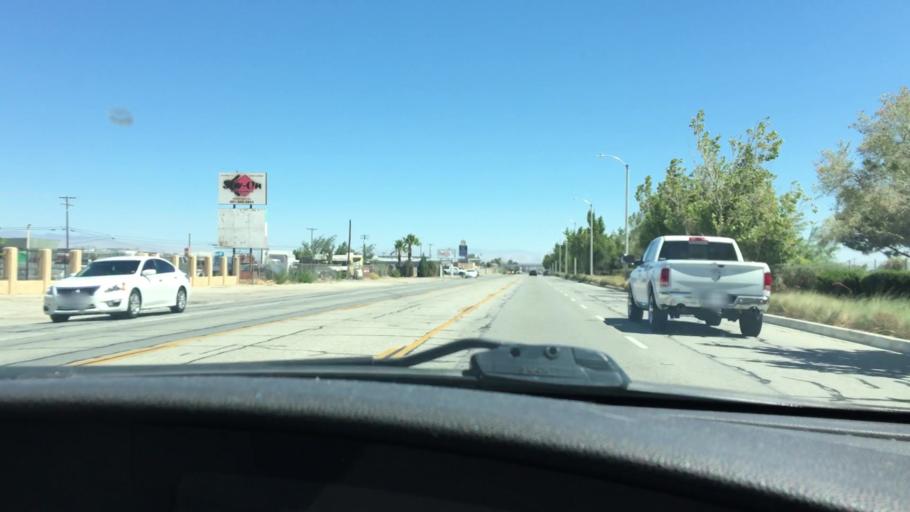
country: US
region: California
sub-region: Los Angeles County
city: Lancaster
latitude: 34.6510
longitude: -118.1291
